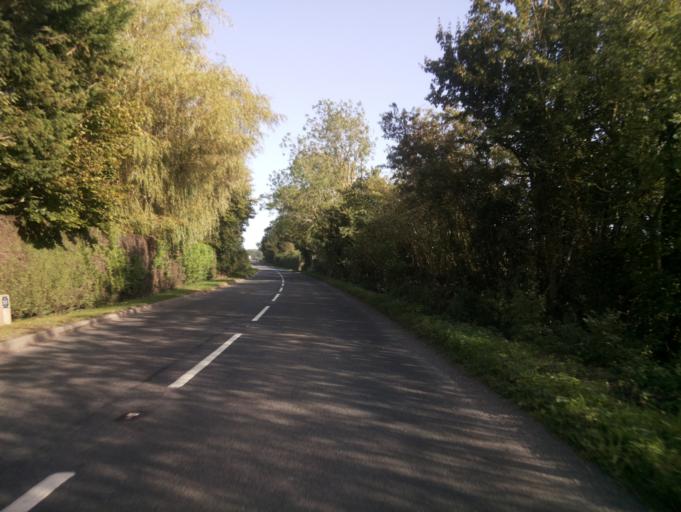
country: GB
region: England
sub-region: Gloucestershire
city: Gloucester
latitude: 51.9619
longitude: -2.2954
